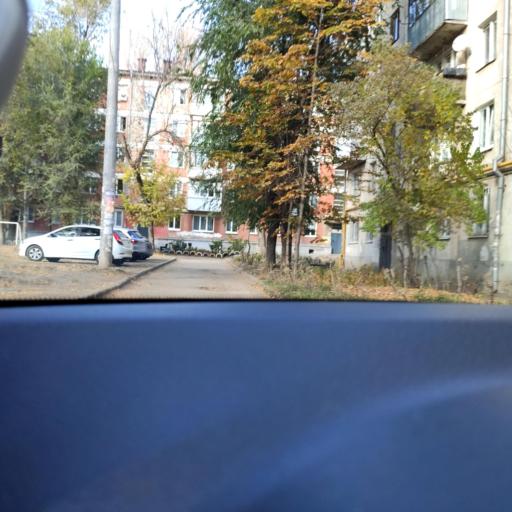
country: RU
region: Samara
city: Samara
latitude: 53.2131
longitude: 50.2561
